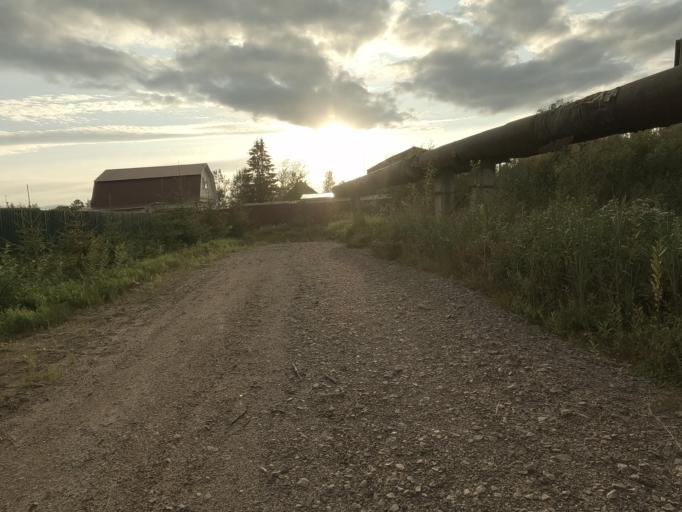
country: RU
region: Leningrad
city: Mga
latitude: 59.7569
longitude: 31.0810
